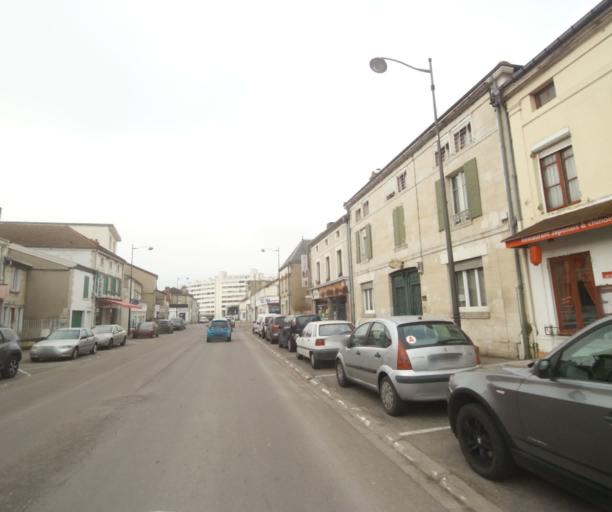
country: FR
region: Champagne-Ardenne
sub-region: Departement de la Haute-Marne
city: Saint-Dizier
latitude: 48.6360
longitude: 4.9595
